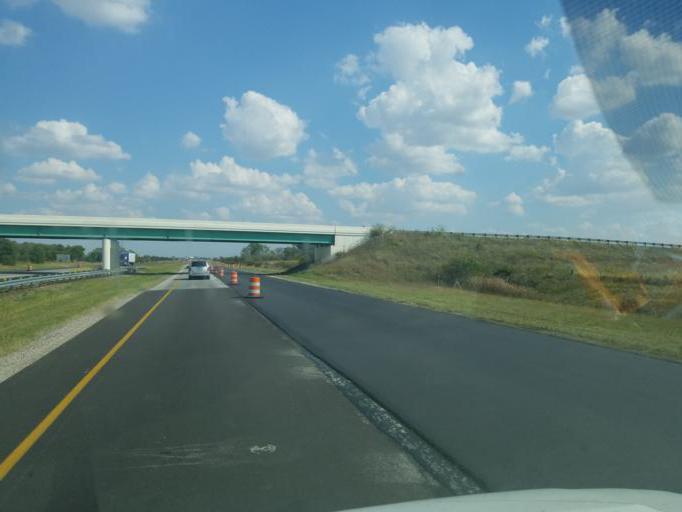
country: US
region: Ohio
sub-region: Van Wert County
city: Van Wert
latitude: 40.8697
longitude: -84.4768
